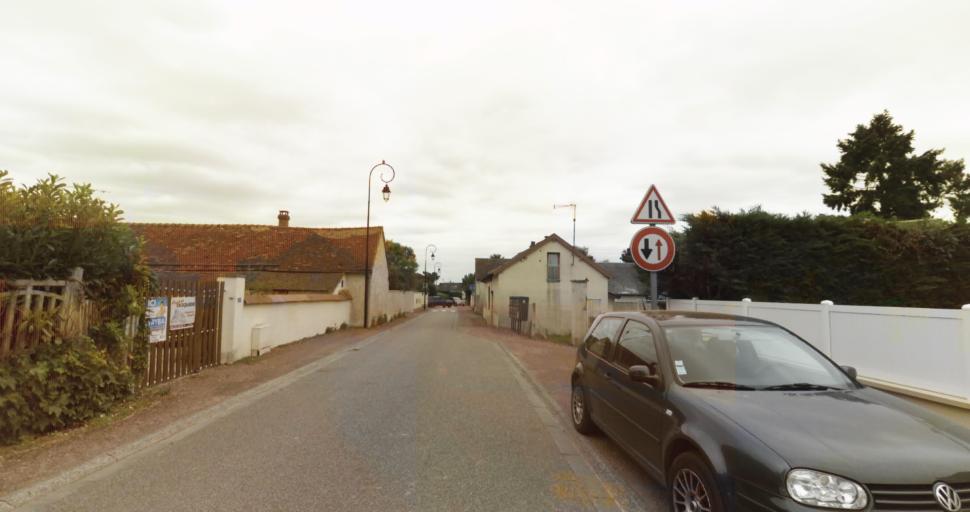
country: FR
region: Haute-Normandie
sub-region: Departement de l'Eure
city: Menilles
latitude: 48.9590
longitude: 1.2935
